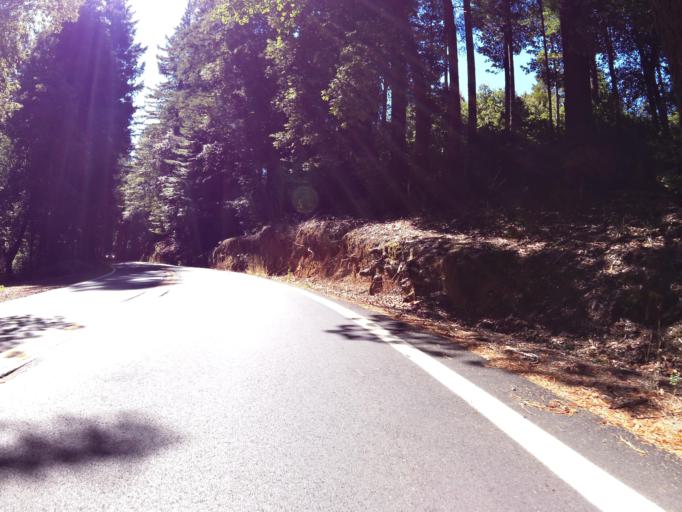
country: US
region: California
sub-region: Humboldt County
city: Redway
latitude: 39.8230
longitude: -123.7809
